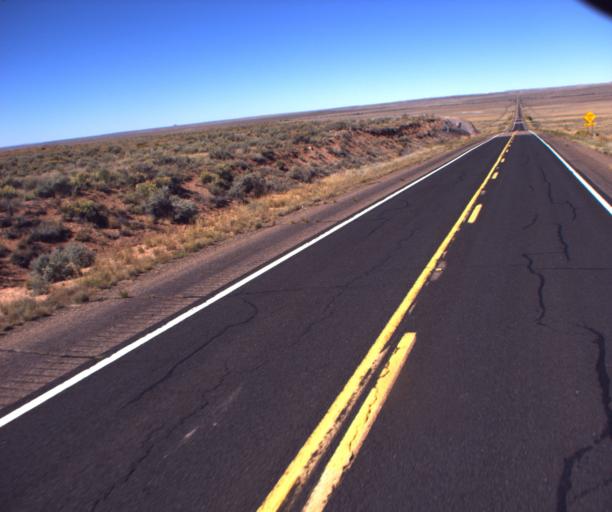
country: US
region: Arizona
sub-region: Navajo County
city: Snowflake
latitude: 34.7159
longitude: -109.7680
